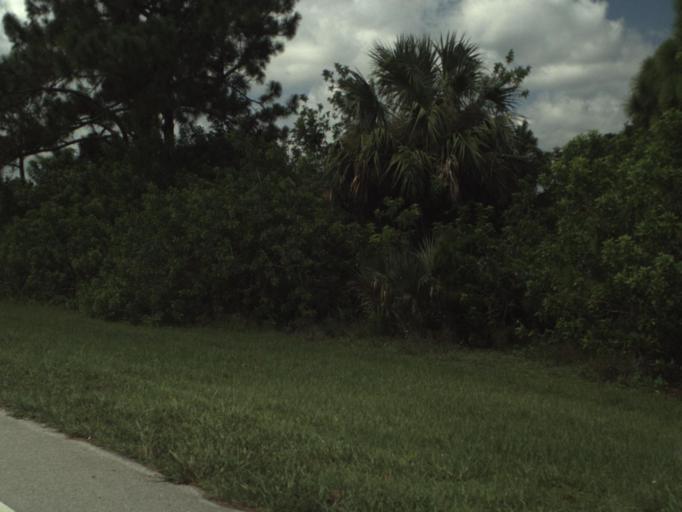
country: US
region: Florida
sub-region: Palm Beach County
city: Jupiter
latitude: 26.8947
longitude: -80.0950
